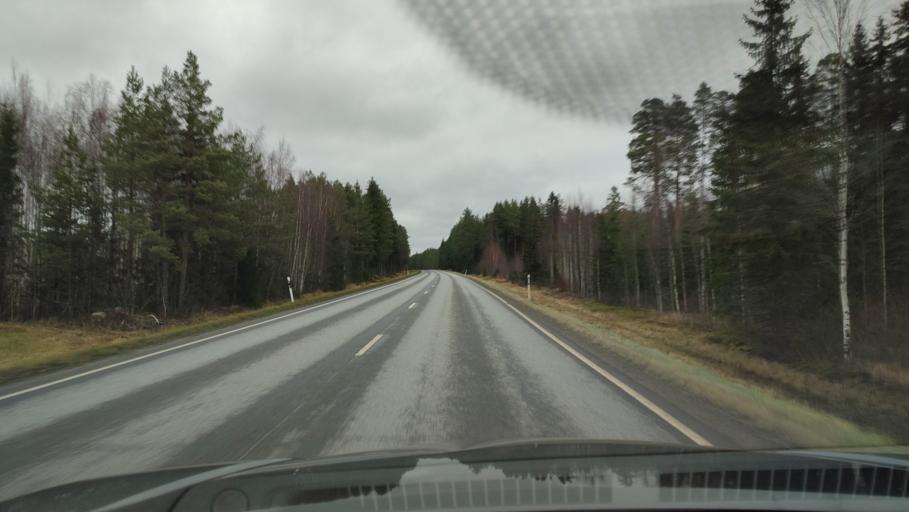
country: FI
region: Southern Ostrobothnia
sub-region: Suupohja
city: Kauhajoki
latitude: 62.4891
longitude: 22.2920
